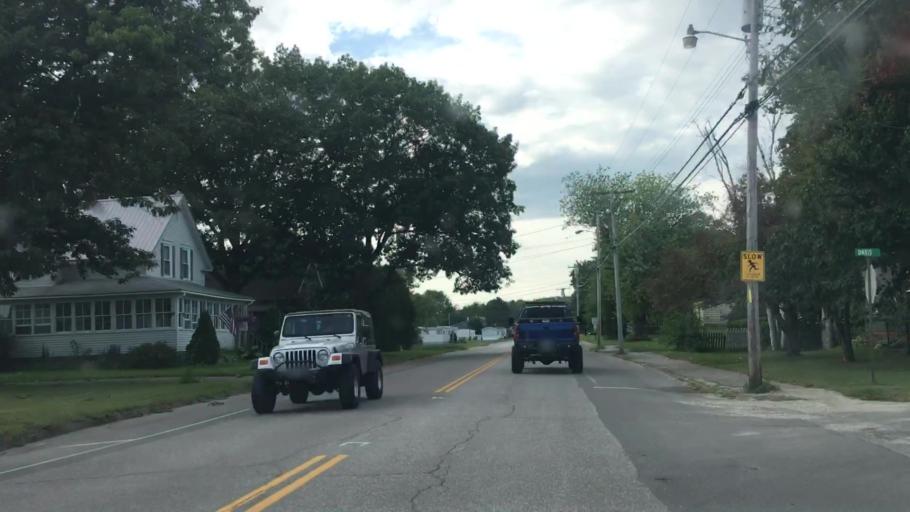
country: US
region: Maine
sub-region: Penobscot County
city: Howland
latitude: 45.2418
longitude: -68.6590
